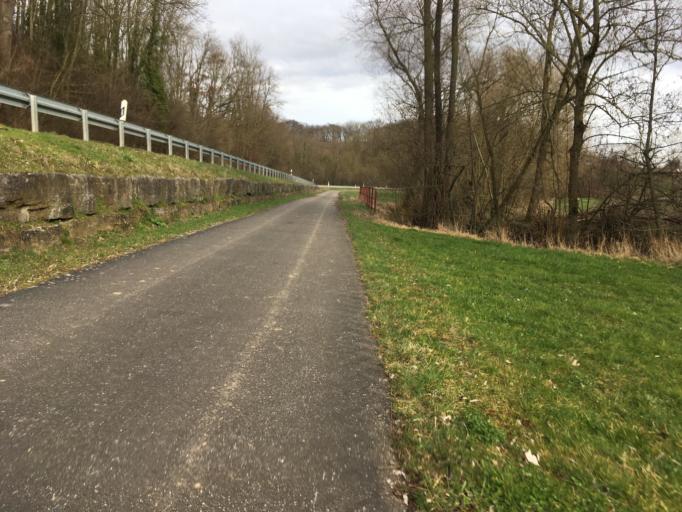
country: DE
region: Baden-Wuerttemberg
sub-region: Regierungsbezirk Stuttgart
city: Bretzfeld
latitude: 49.2068
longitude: 9.4248
